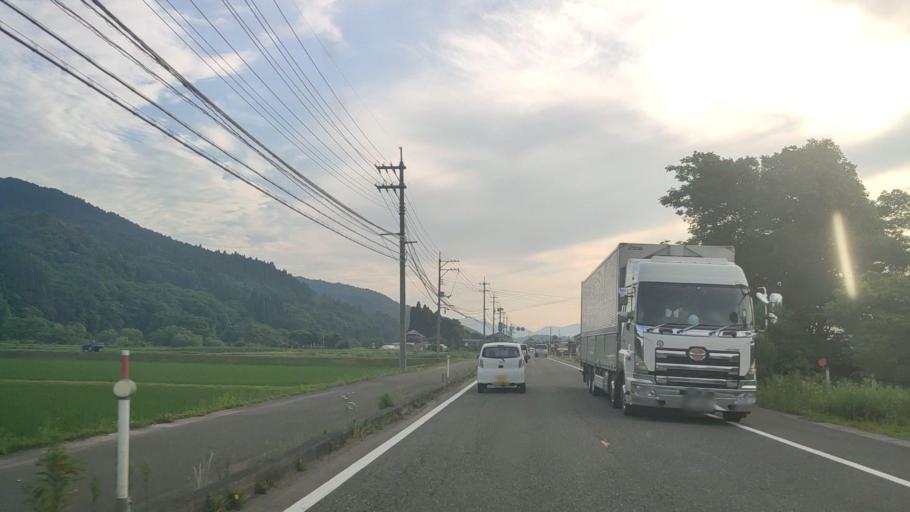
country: JP
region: Tottori
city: Kurayoshi
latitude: 35.2911
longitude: 133.7260
